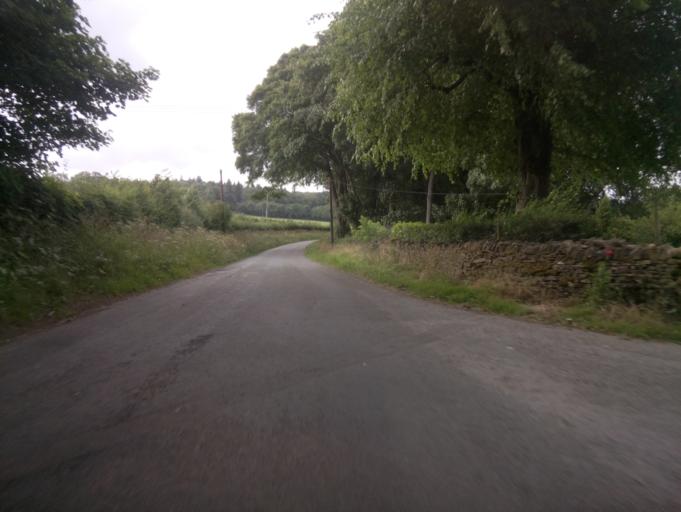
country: GB
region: England
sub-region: Gloucestershire
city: Donnington
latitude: 51.9759
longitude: -1.7546
